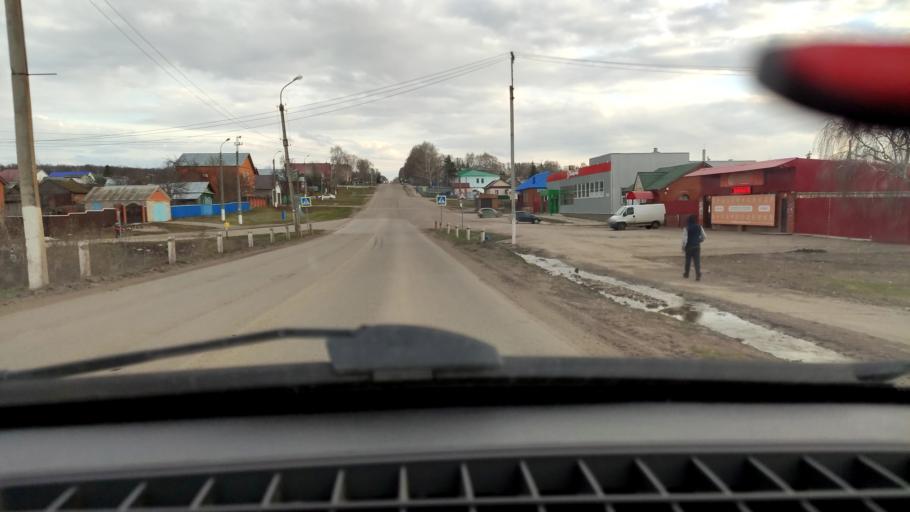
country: RU
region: Bashkortostan
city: Tolbazy
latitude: 54.0231
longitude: 55.8863
